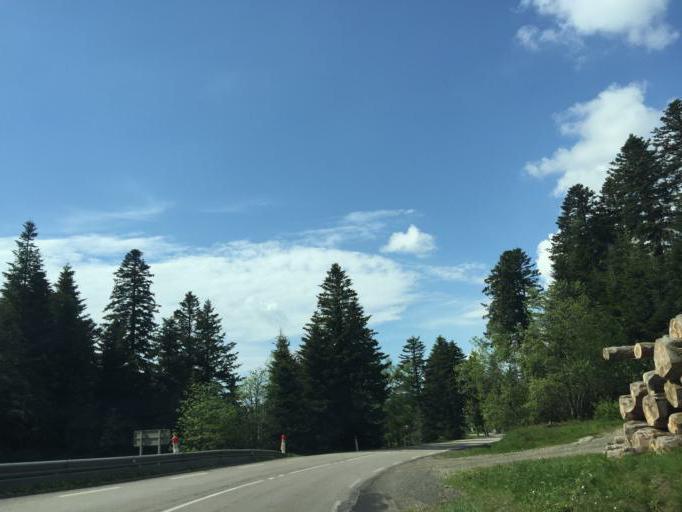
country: FR
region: Rhone-Alpes
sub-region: Departement de la Loire
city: Saint-Genest-Malifaux
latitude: 45.3459
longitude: 4.4821
